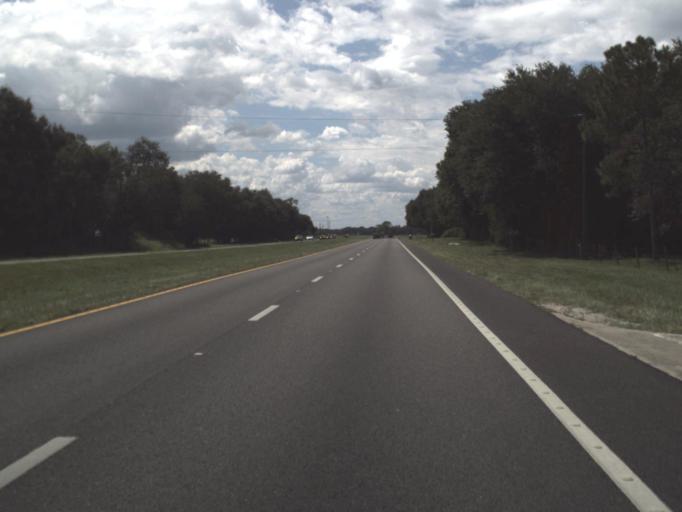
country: US
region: Florida
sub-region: Polk County
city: Alturas
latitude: 27.9092
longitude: -81.6794
